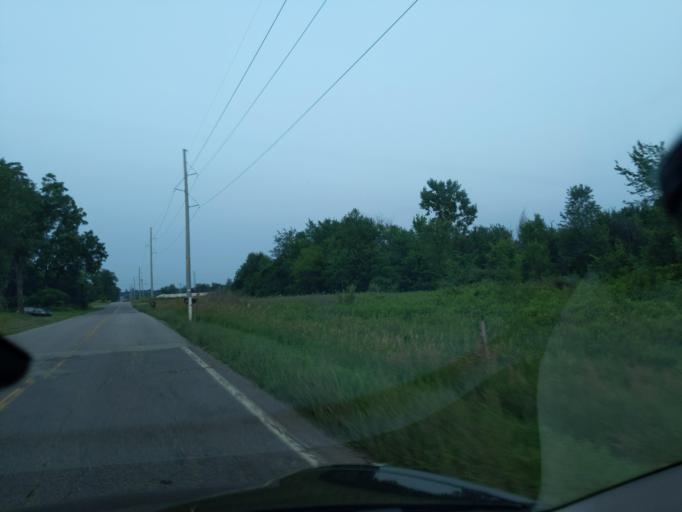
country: US
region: Michigan
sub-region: Jackson County
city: Jackson
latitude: 42.3275
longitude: -84.4503
